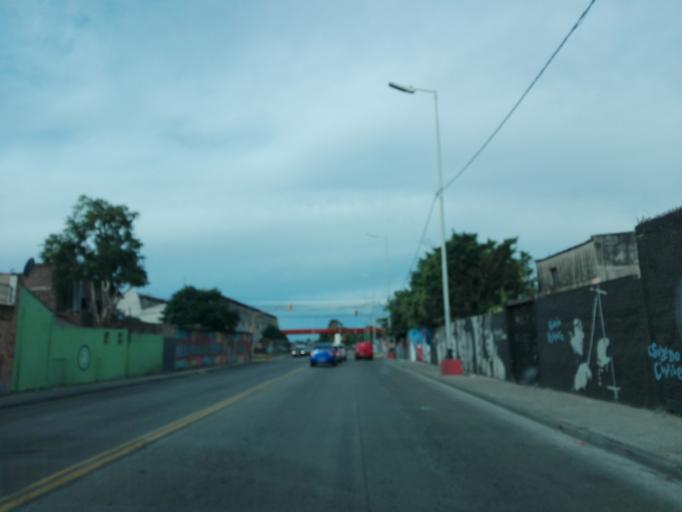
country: AR
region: Buenos Aires
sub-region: Partido de Avellaneda
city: Avellaneda
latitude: -34.6815
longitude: -58.3422
